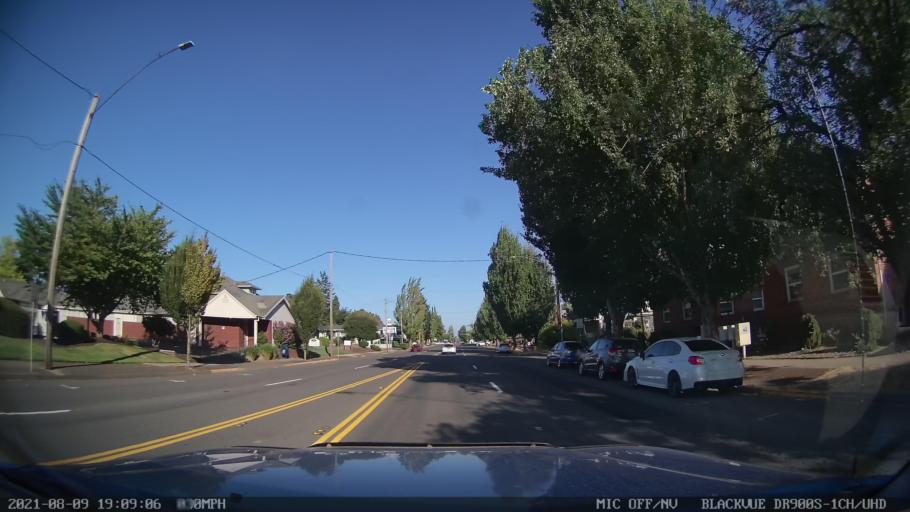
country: US
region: Oregon
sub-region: Marion County
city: Salem
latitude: 44.9360
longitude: -123.0235
